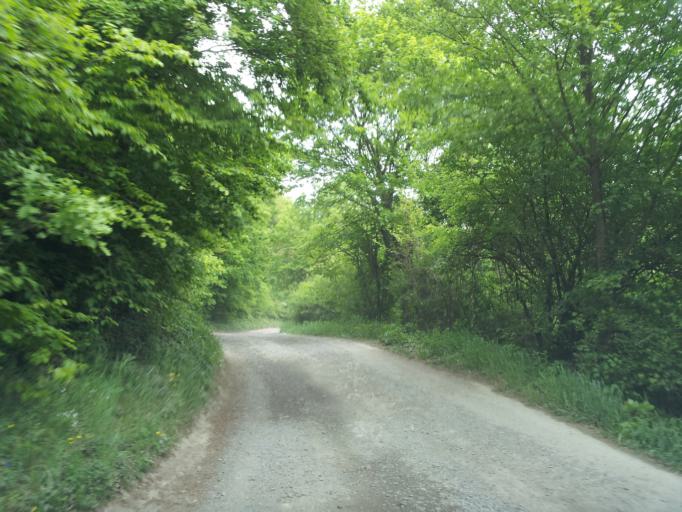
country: HU
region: Baranya
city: Hosszuheteny
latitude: 46.1754
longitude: 18.3482
